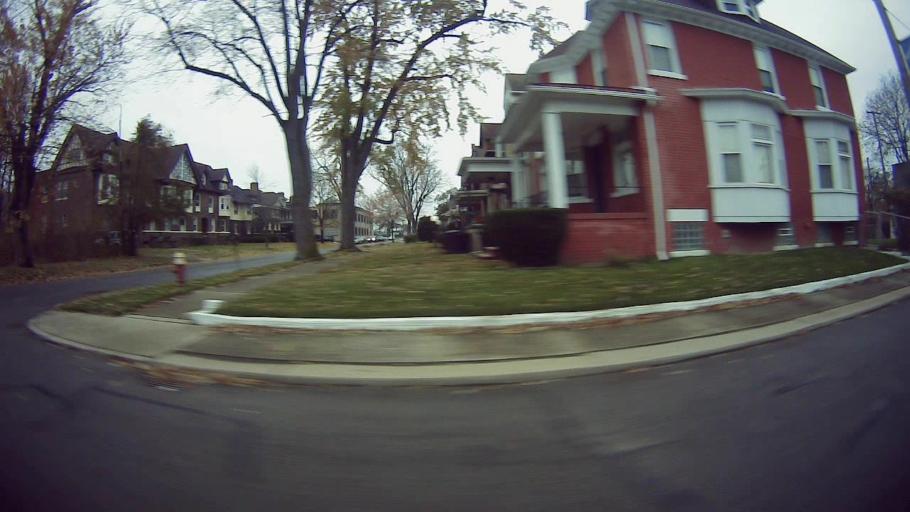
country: US
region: Michigan
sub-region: Wayne County
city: Hamtramck
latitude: 42.3797
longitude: -83.0769
